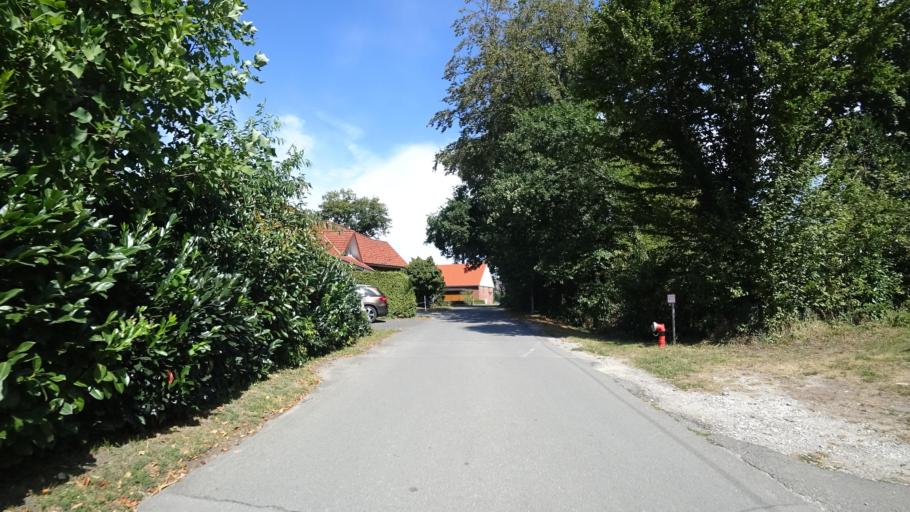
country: DE
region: North Rhine-Westphalia
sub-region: Regierungsbezirk Detmold
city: Steinhagen
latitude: 51.9545
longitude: 8.3856
